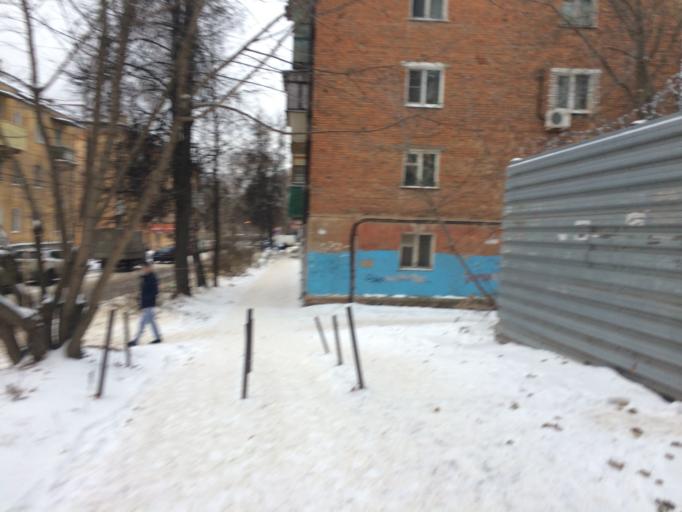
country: RU
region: Tula
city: Mendeleyevskiy
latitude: 54.1693
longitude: 37.5879
